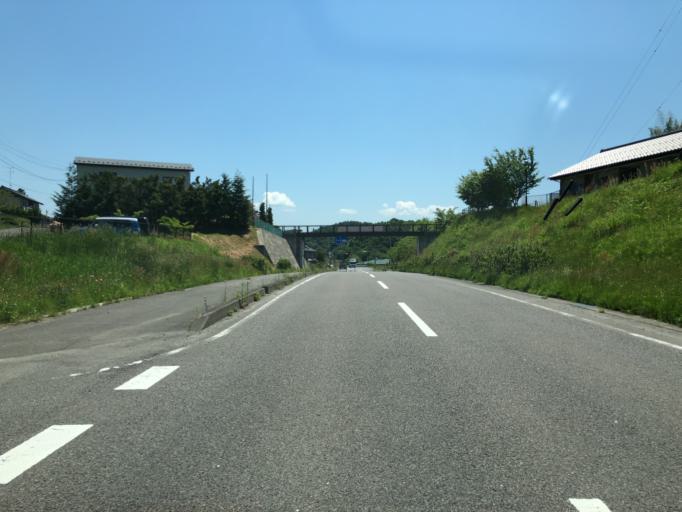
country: JP
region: Fukushima
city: Motomiya
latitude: 37.5261
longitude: 140.4423
